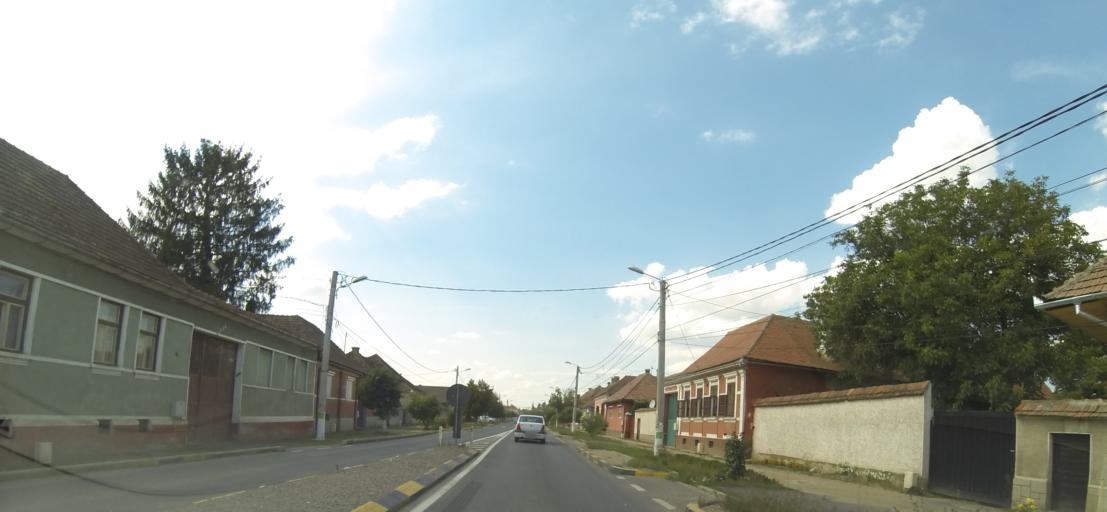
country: RO
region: Brasov
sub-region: Comuna Sercaia
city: Sercaia
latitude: 45.8297
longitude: 25.1471
